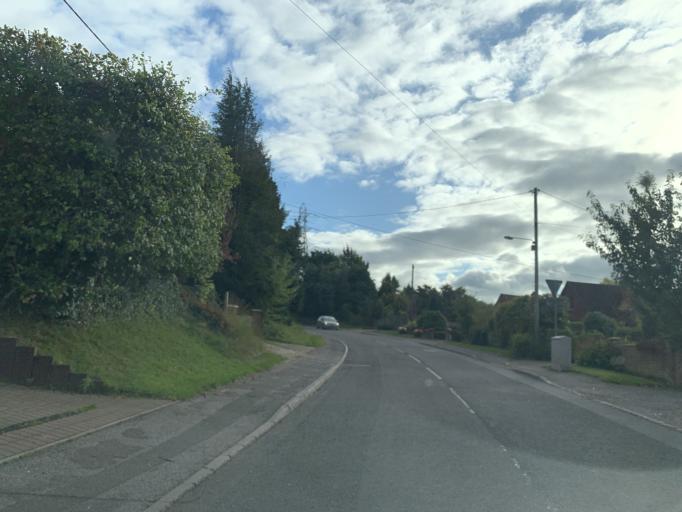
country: GB
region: England
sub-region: Wiltshire
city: Bulford
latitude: 51.1882
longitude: -1.7608
